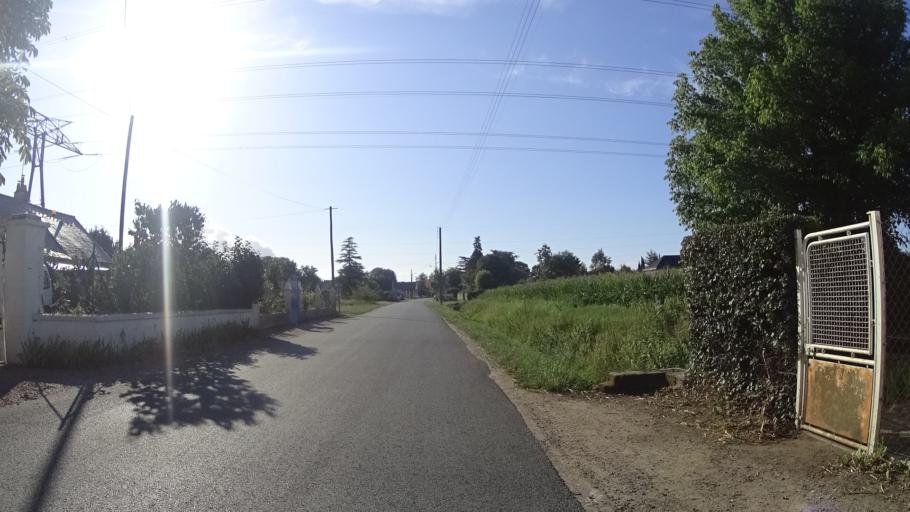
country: FR
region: Pays de la Loire
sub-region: Departement de Maine-et-Loire
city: Varennes-sur-Loire
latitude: 47.2406
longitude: 0.0486
